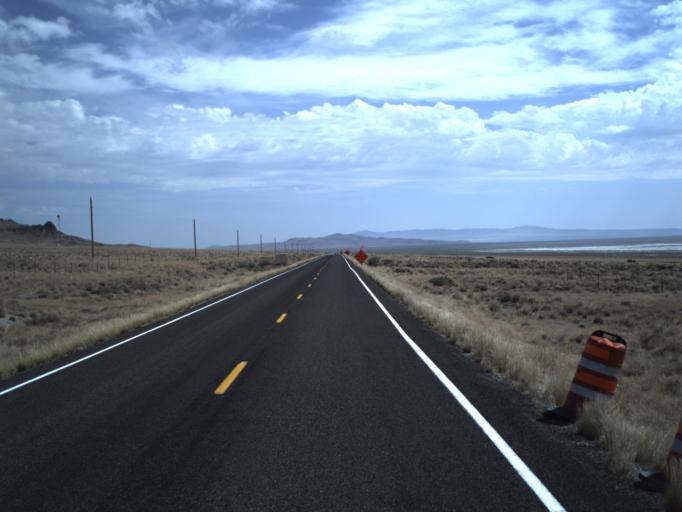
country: US
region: Utah
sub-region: Tooele County
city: Wendover
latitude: 41.4390
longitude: -113.7219
